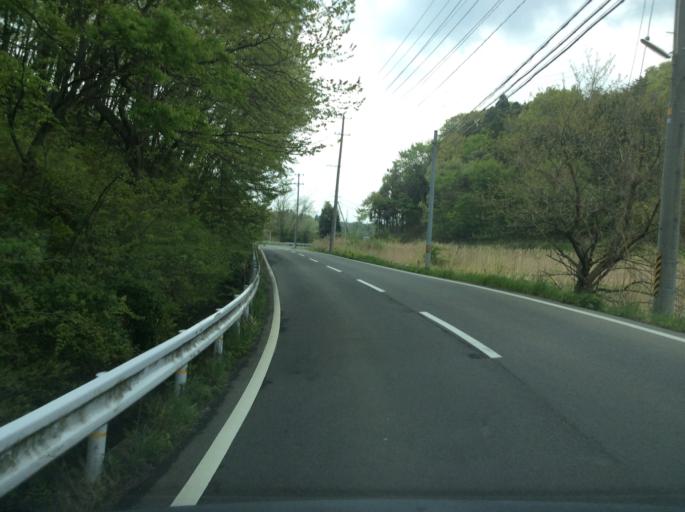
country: JP
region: Fukushima
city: Koriyama
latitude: 37.3889
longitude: 140.4277
